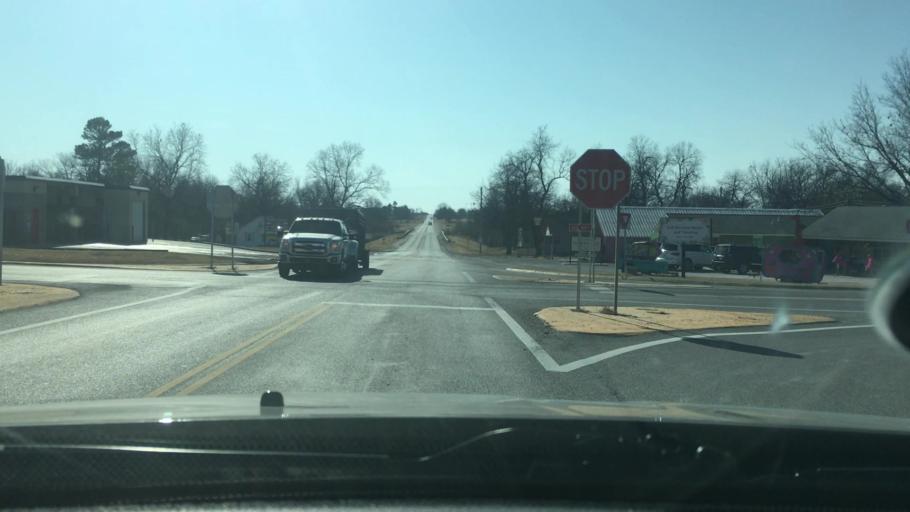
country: US
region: Oklahoma
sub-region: Garvin County
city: Stratford
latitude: 34.7968
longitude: -96.9677
